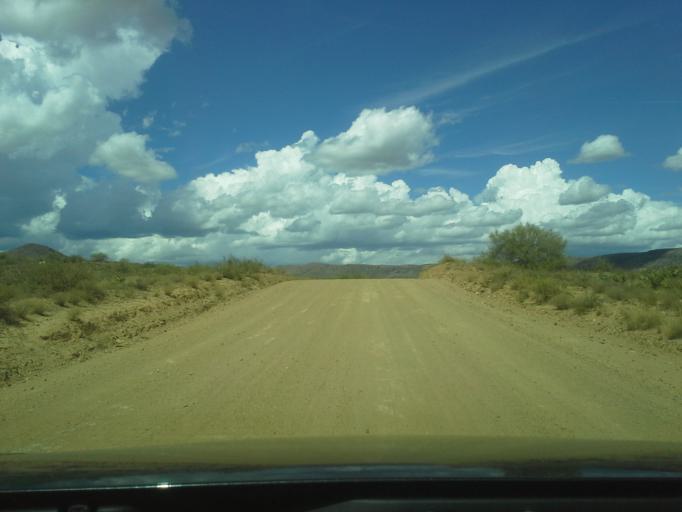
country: US
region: Arizona
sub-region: Yavapai County
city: Spring Valley
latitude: 34.2690
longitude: -112.1920
